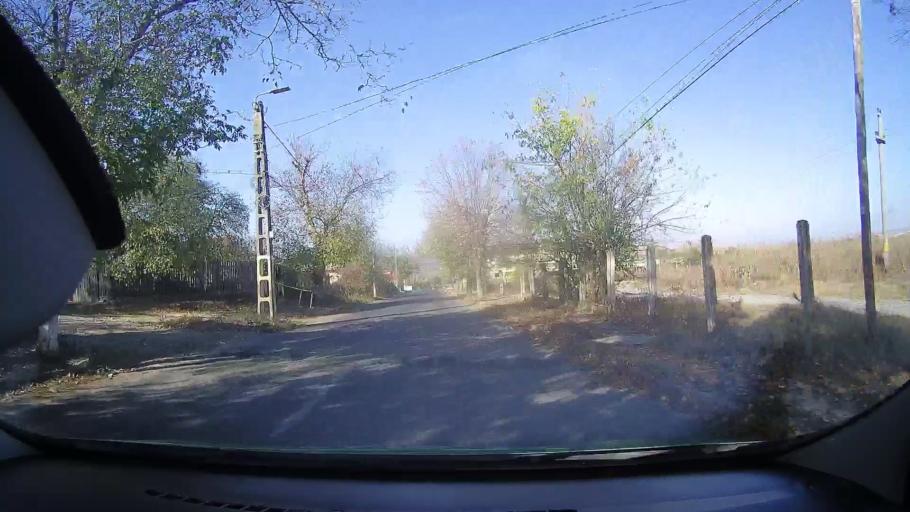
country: RO
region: Tulcea
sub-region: Oras Babadag
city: Babadag
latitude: 44.8864
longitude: 28.7346
